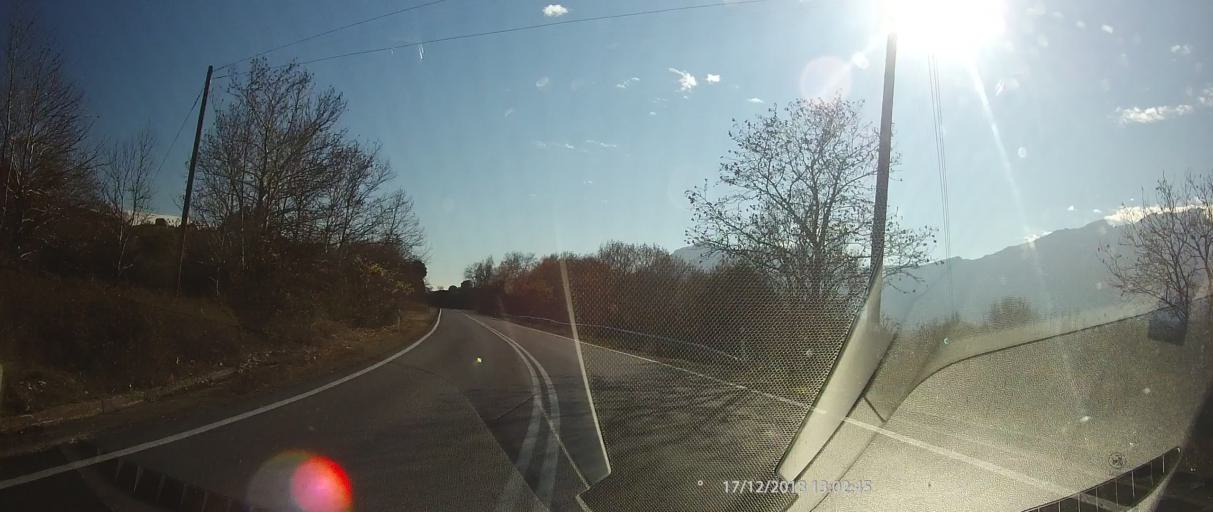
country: GR
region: Thessaly
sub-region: Trikala
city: Kastraki
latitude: 39.7195
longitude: 21.5949
